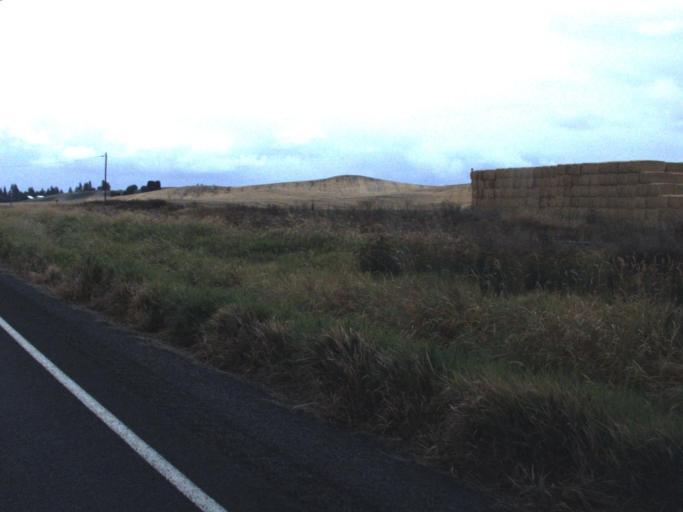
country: US
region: Washington
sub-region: Whitman County
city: Colfax
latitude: 47.1465
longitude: -117.2565
